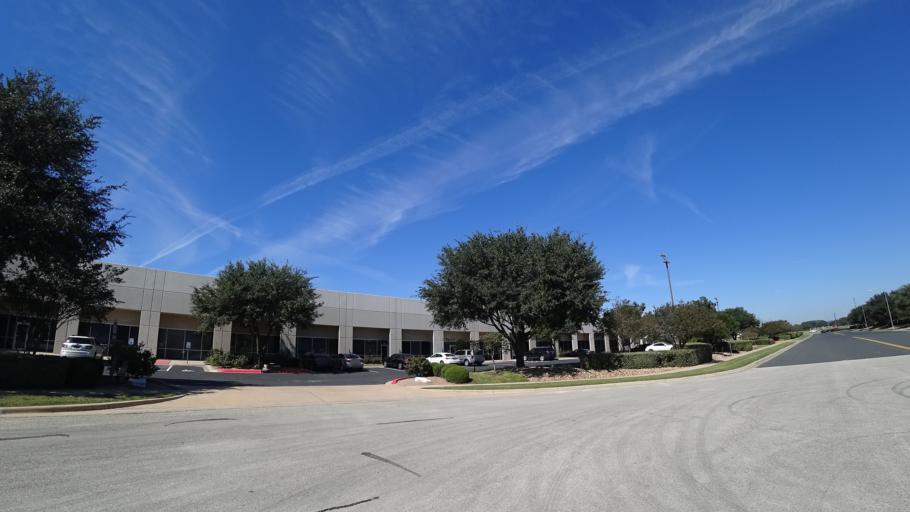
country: US
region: Texas
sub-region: Travis County
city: Austin
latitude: 30.2103
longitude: -97.7209
